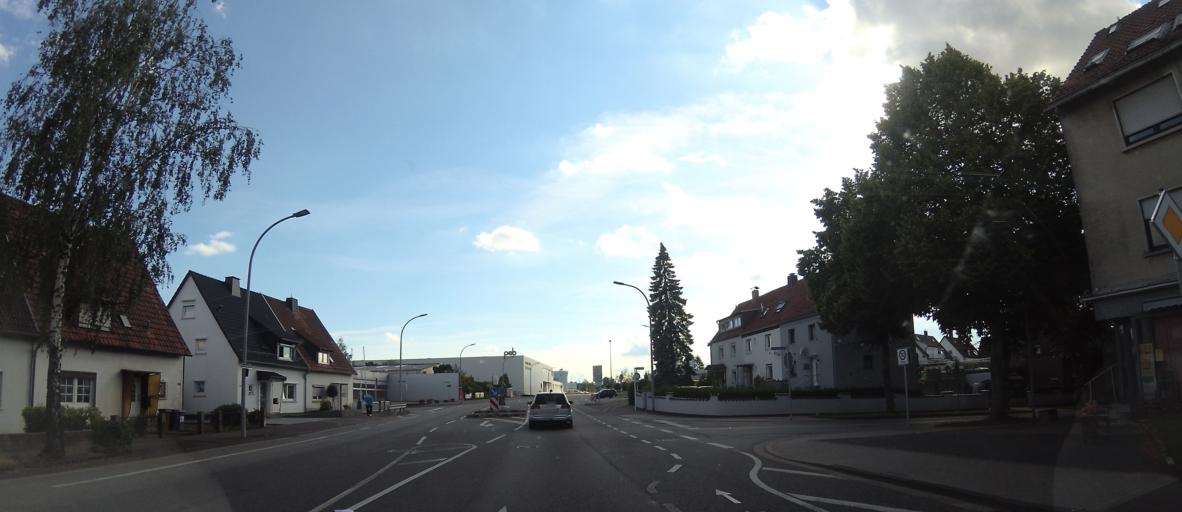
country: DE
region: Rheinland-Pfalz
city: Pirmasens
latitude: 49.1888
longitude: 7.5935
